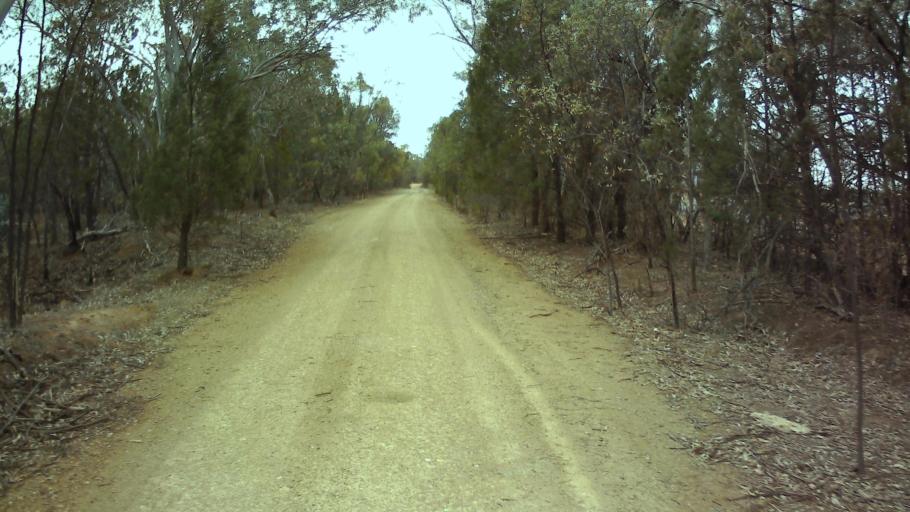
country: AU
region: New South Wales
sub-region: Weddin
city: Grenfell
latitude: -33.8878
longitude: 148.1572
